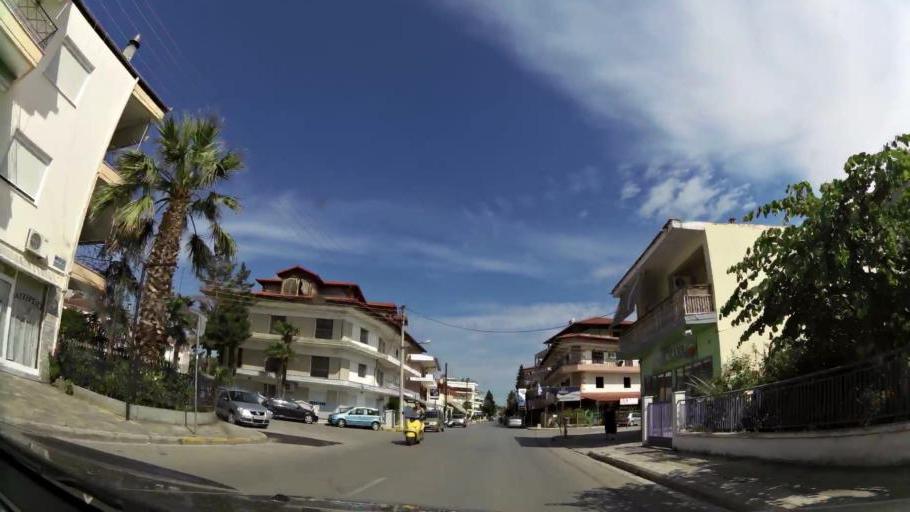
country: GR
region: Central Macedonia
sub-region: Nomos Pierias
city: Katerini
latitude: 40.2785
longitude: 22.5046
